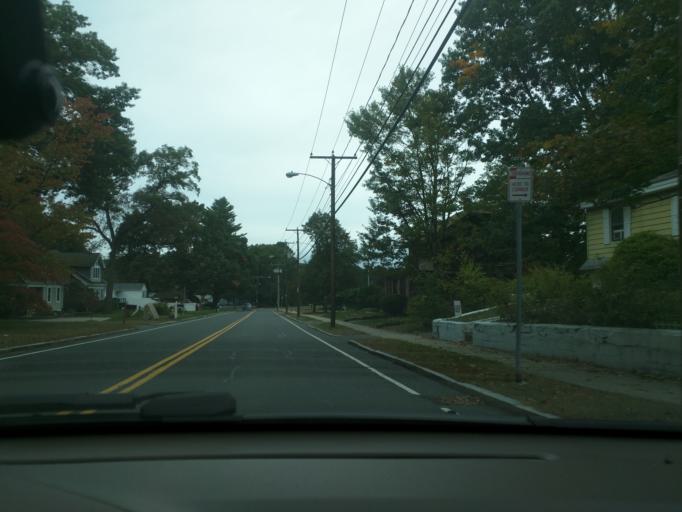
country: US
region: Massachusetts
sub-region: Hampden County
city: East Longmeadow
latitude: 42.0724
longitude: -72.5447
